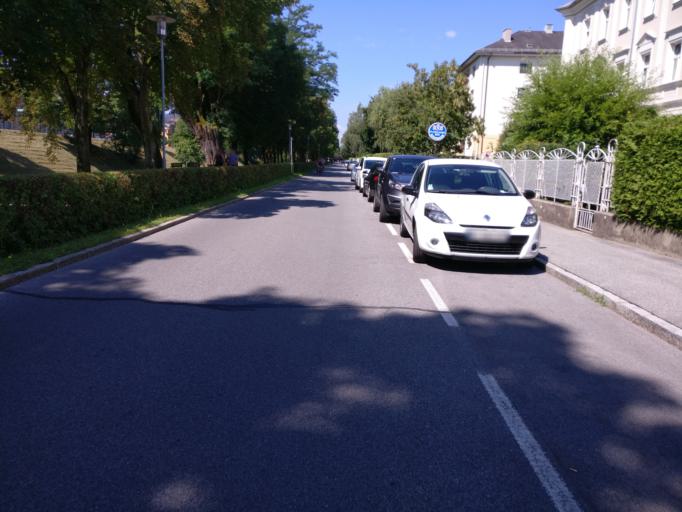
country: AT
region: Carinthia
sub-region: Klagenfurt am Woerthersee
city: Klagenfurt am Woerthersee
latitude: 46.6221
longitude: 14.2913
